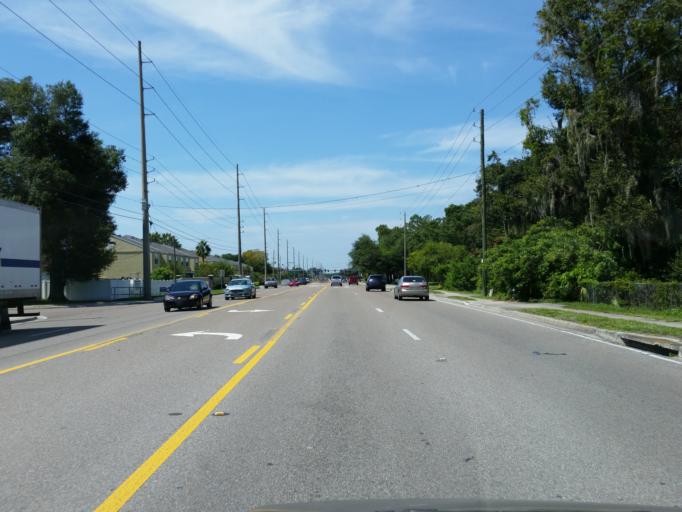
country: US
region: Florida
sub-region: Hillsborough County
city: Riverview
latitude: 27.8937
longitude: -82.3267
